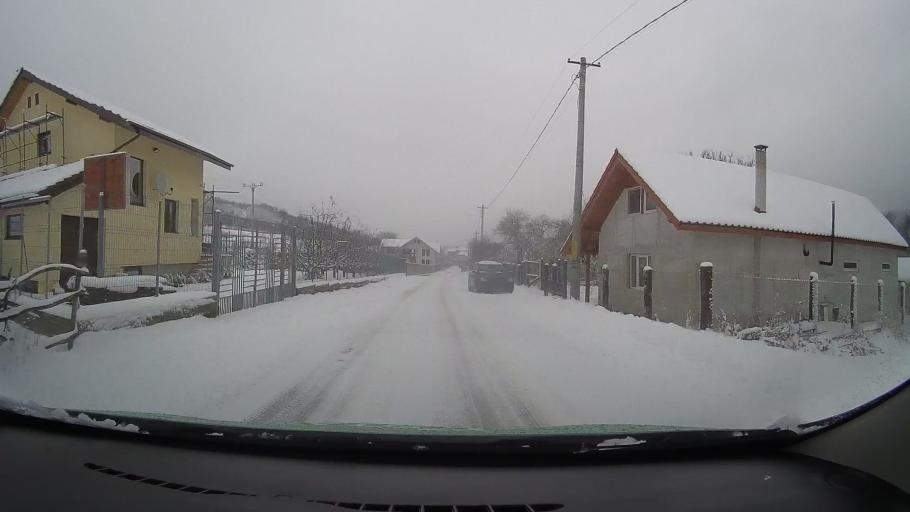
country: RO
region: Hunedoara
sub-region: Comuna Carjiti
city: Carjiti
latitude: 45.8297
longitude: 22.8454
